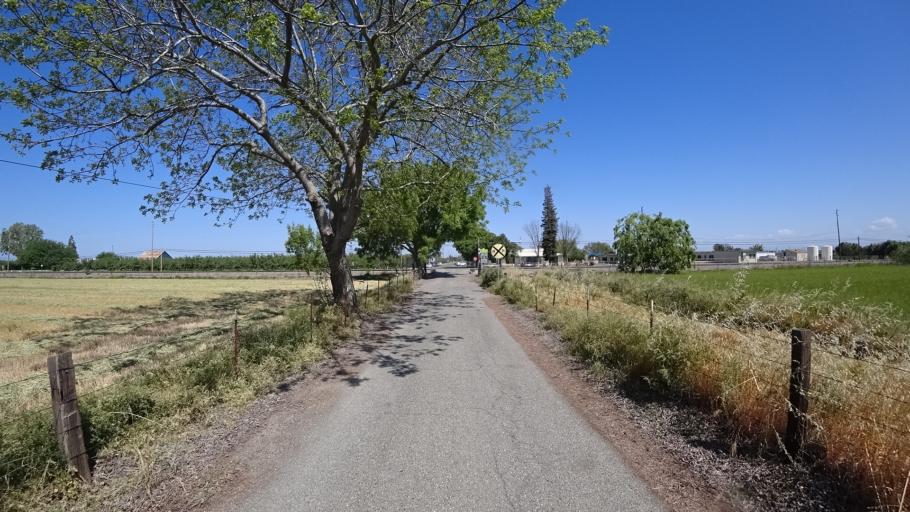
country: US
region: California
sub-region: Glenn County
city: Orland
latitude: 39.7679
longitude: -122.1595
